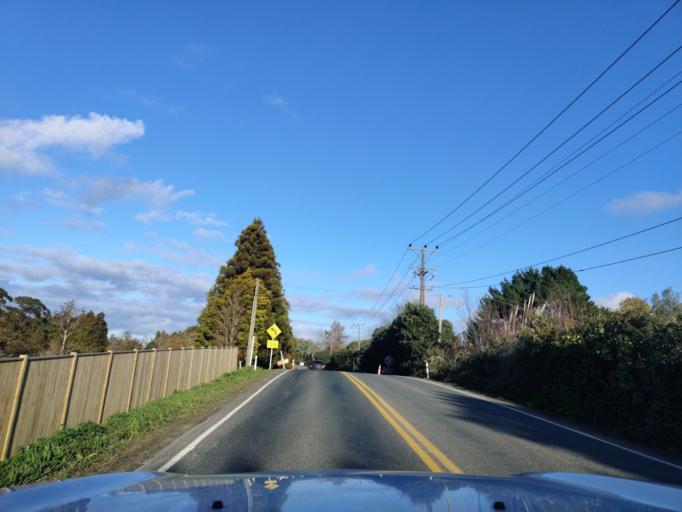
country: NZ
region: Auckland
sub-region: Auckland
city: Red Hill
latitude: -36.9718
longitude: 174.9861
